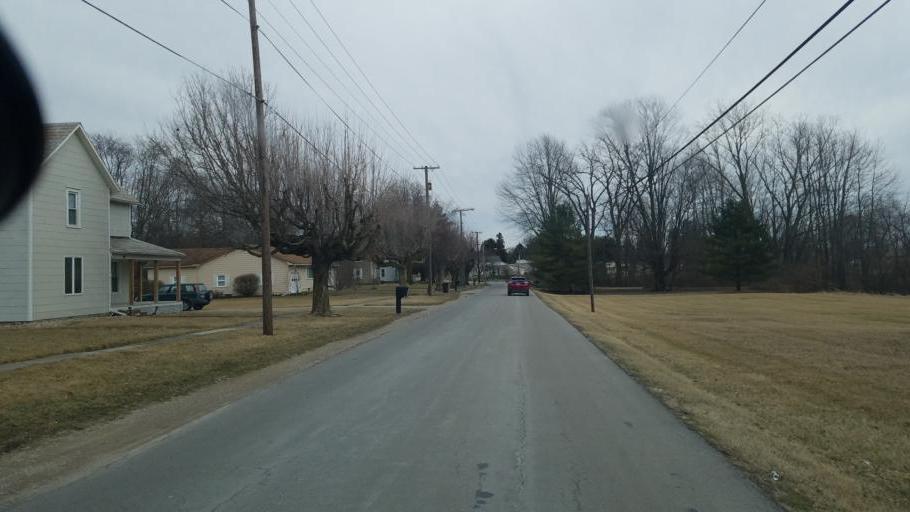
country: US
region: Ohio
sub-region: Marion County
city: Prospect
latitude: 40.4579
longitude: -83.0851
